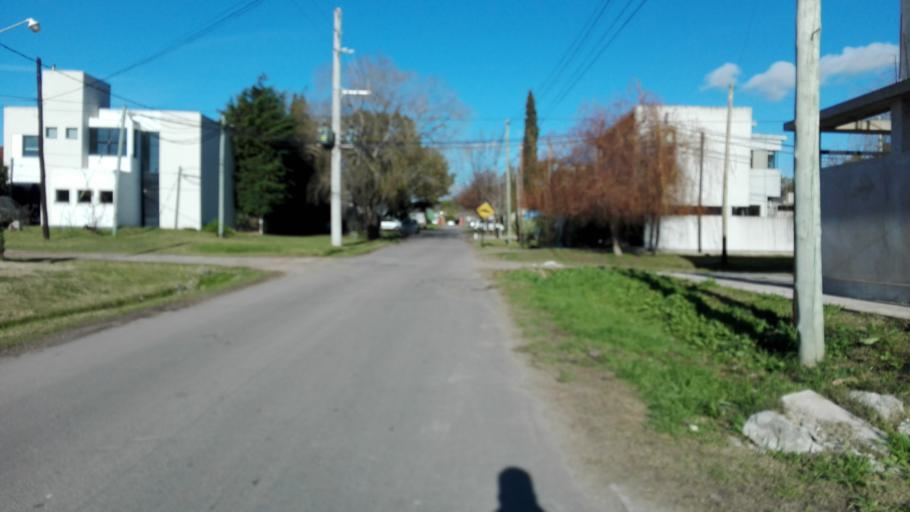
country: AR
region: Buenos Aires
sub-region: Partido de La Plata
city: La Plata
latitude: -34.8965
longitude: -58.0225
